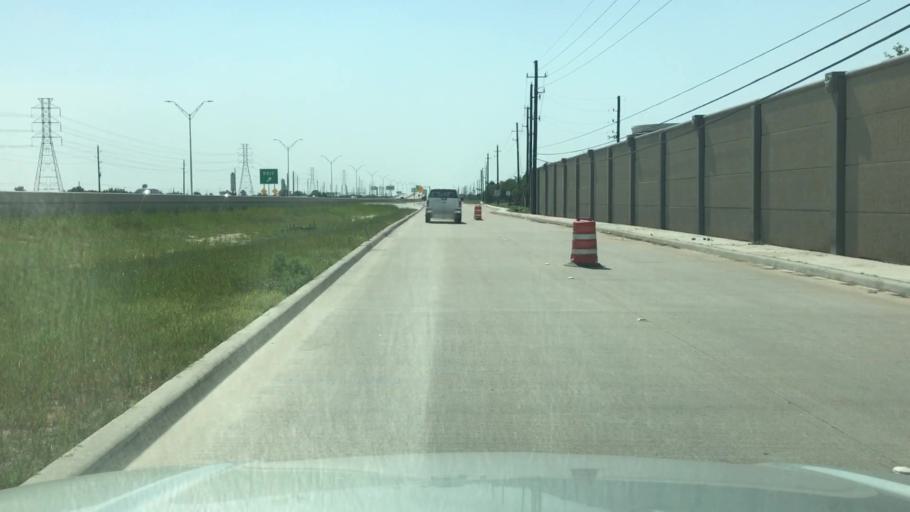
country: US
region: Texas
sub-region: Fort Bend County
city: Cinco Ranch
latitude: 29.6986
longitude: -95.8027
